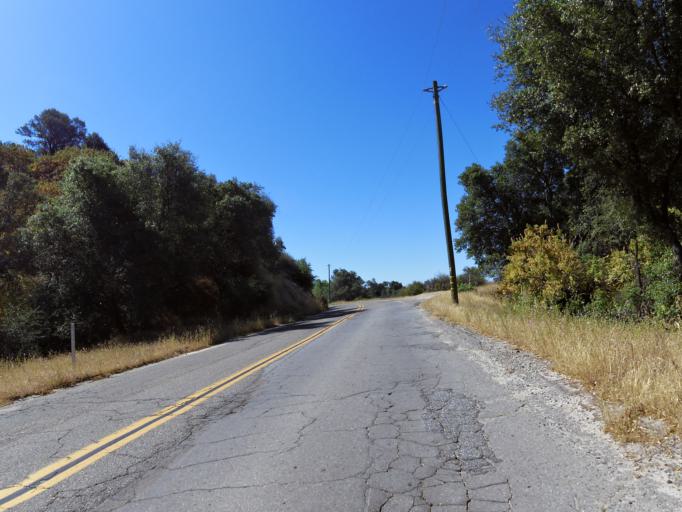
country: US
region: California
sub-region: Fresno County
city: Auberry
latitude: 37.2138
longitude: -119.4806
